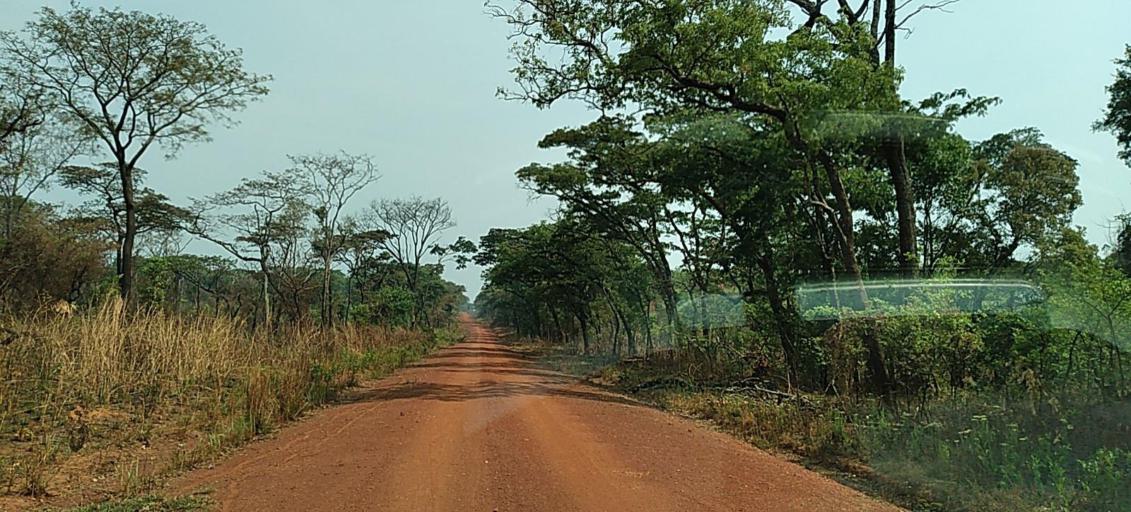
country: ZM
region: North-Western
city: Kansanshi
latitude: -12.0175
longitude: 26.8484
